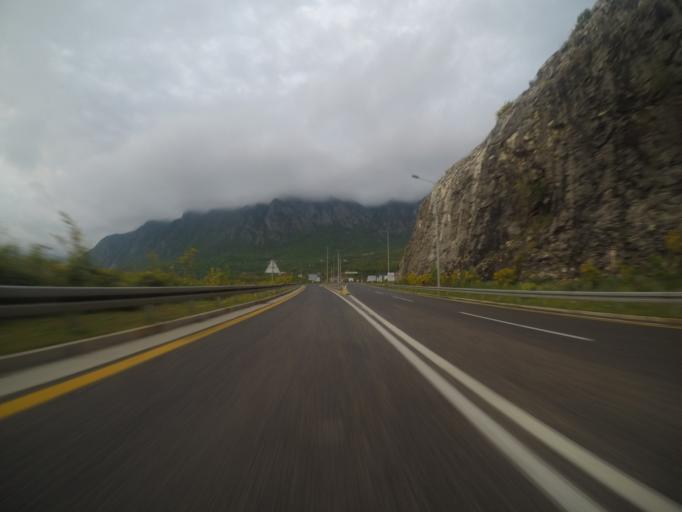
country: ME
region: Bar
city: Sutomore
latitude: 42.2054
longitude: 19.0503
